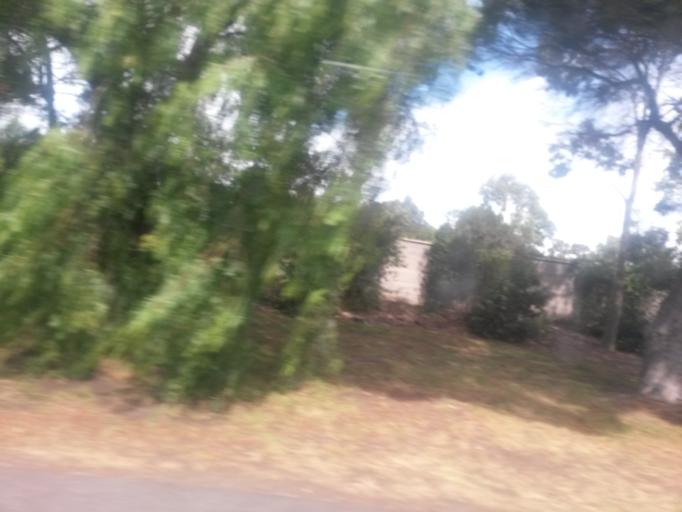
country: AU
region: Victoria
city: Albert Park
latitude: -37.8304
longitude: 145.0076
